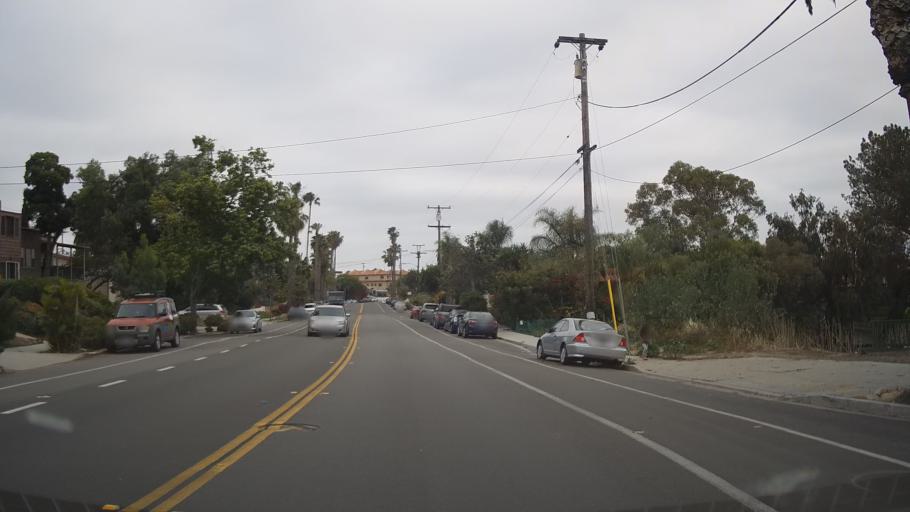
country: US
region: California
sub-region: San Diego County
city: San Diego
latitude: 32.7554
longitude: -117.1513
